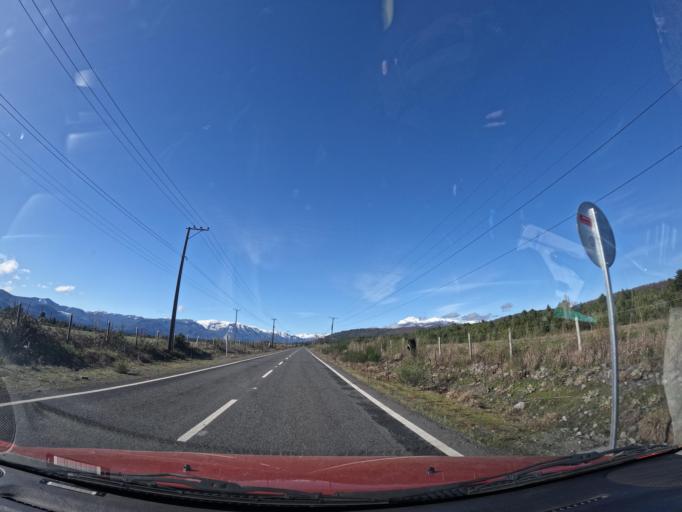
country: CL
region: Biobio
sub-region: Provincia de Biobio
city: Los Angeles
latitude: -37.3383
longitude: -71.7901
